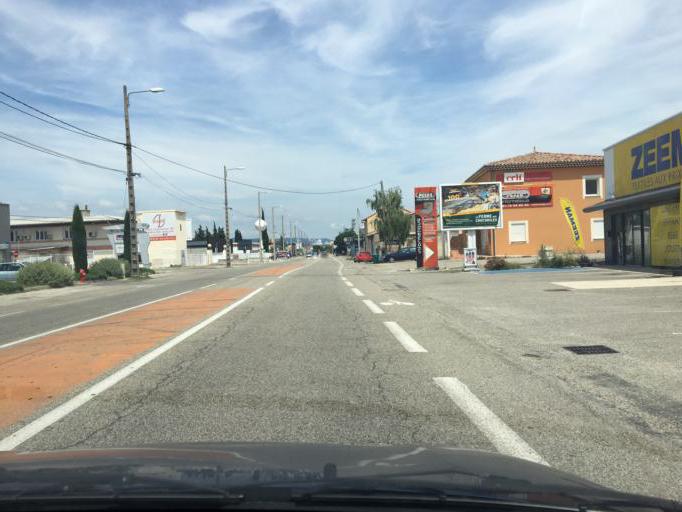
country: FR
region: Rhone-Alpes
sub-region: Departement de la Drome
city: Montelimar
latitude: 44.5383
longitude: 4.7463
